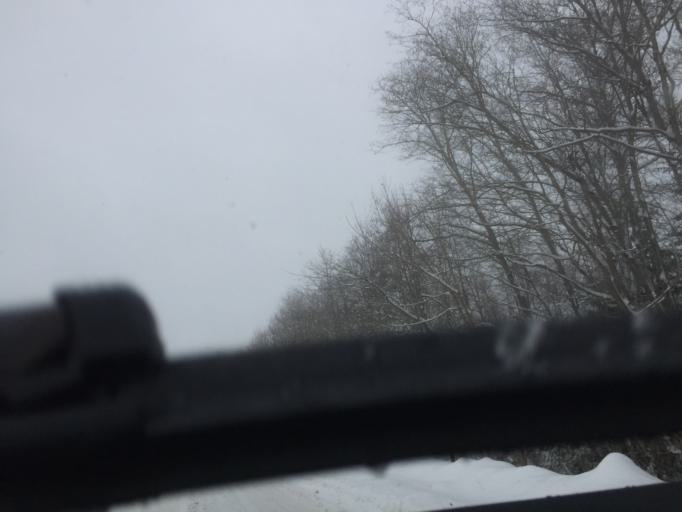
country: LV
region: Amatas Novads
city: Drabesi
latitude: 57.0808
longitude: 25.3436
